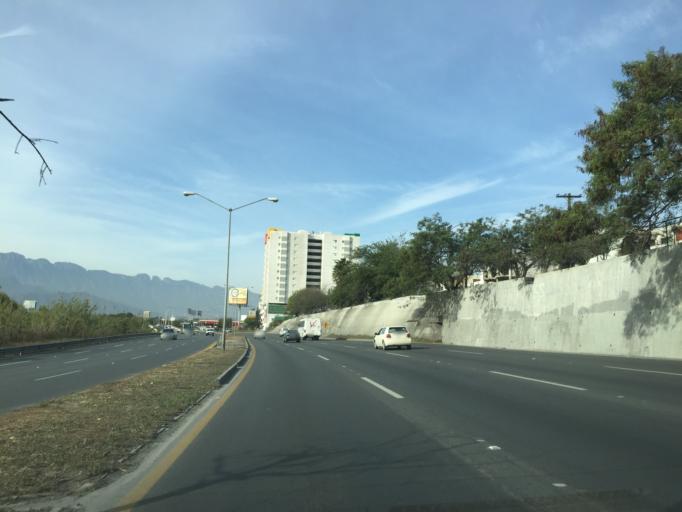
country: MX
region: Nuevo Leon
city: Guadalupe
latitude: 25.6921
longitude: -100.2347
